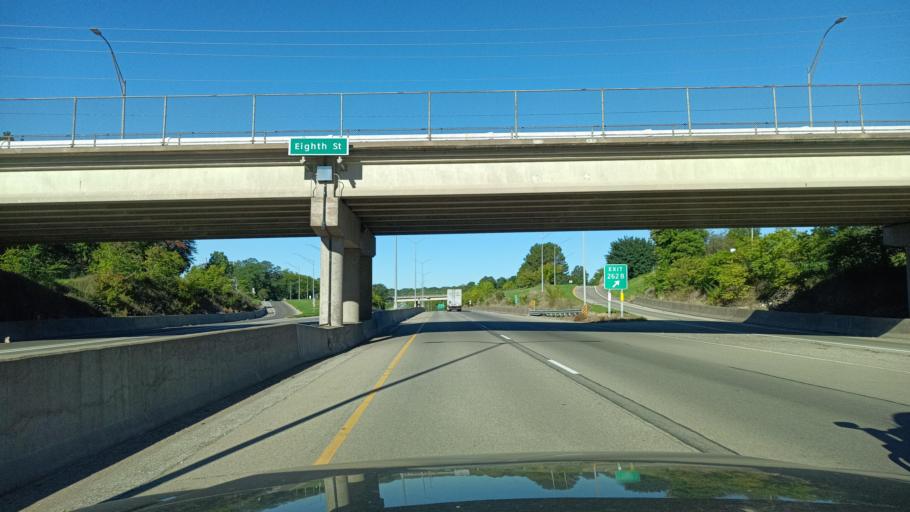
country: US
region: Iowa
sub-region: Des Moines County
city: Burlington
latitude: 40.8151
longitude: -91.1065
